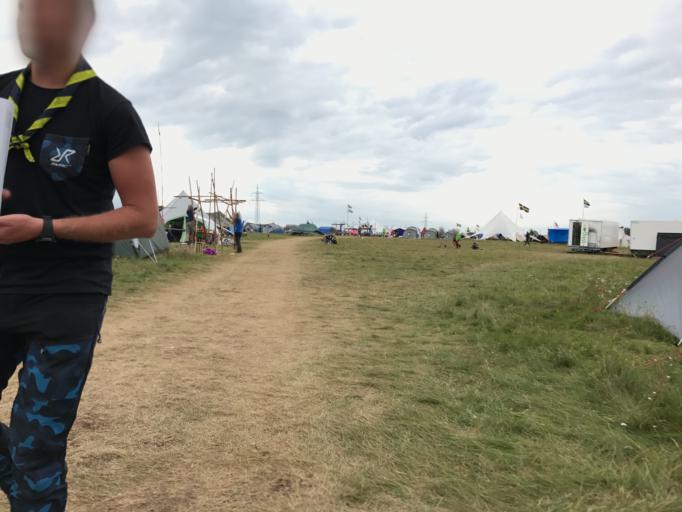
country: SE
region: Skane
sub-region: Kristianstads Kommun
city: Fjalkinge
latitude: 56.0038
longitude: 14.3039
